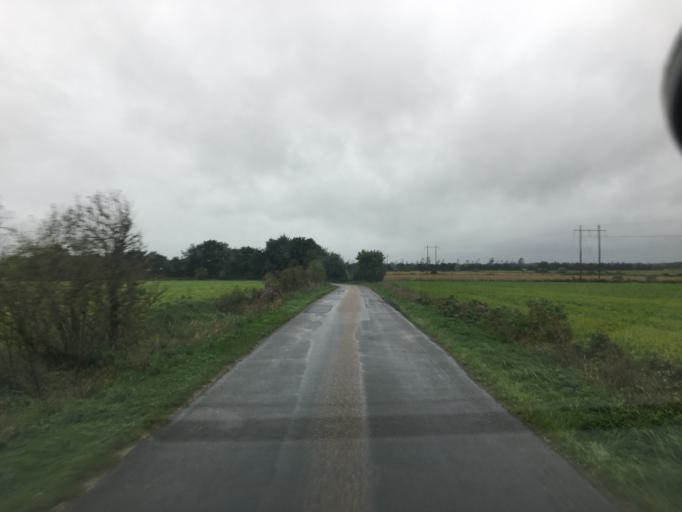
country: DE
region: Schleswig-Holstein
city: Ladelund
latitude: 54.9557
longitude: 9.0291
